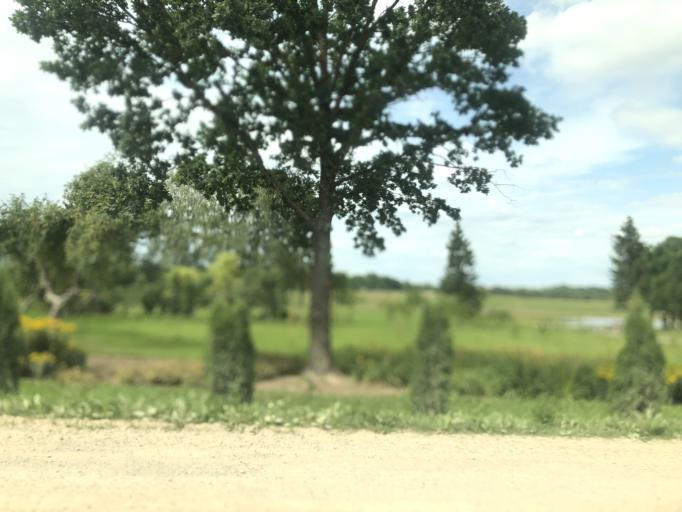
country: LV
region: Vecumnieki
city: Vecumnieki
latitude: 56.4616
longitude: 24.6167
